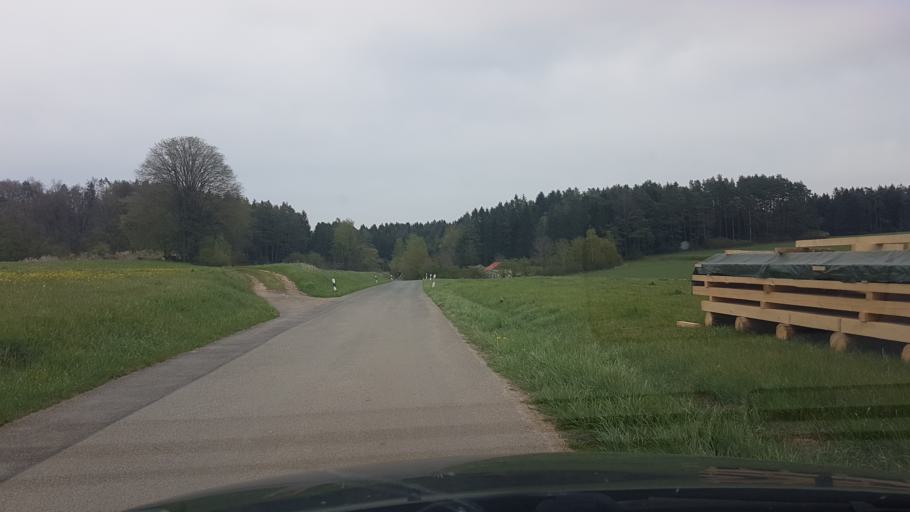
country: DE
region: Bavaria
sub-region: Upper Franconia
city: Stadelhofen
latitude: 50.0045
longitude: 11.1577
